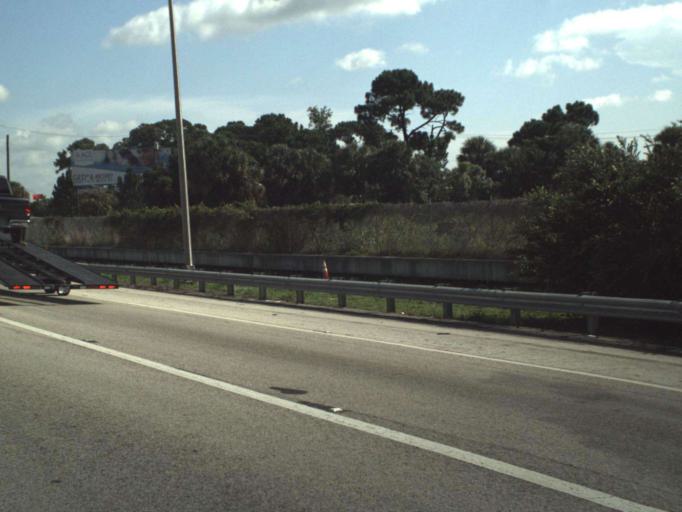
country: US
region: Florida
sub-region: Palm Beach County
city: Mangonia Park
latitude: 26.7787
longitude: -80.0986
